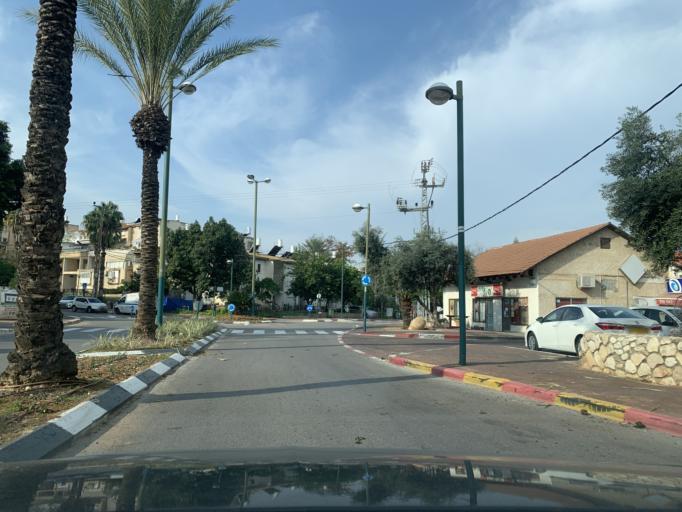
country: IL
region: Central District
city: Kfar Saba
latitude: 32.1903
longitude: 34.9018
